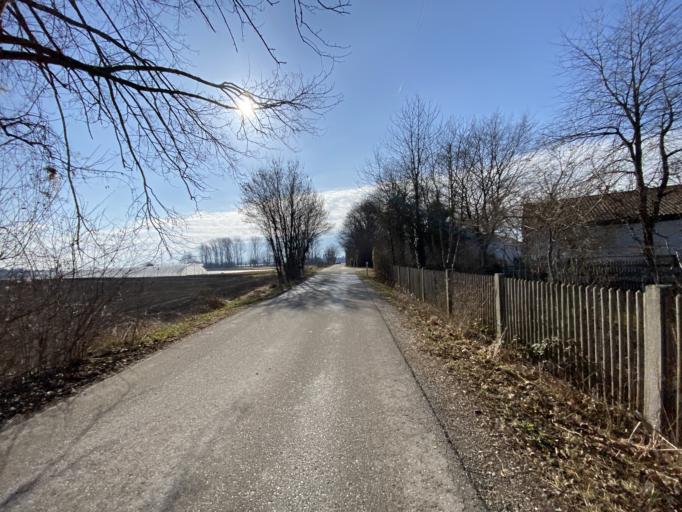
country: DE
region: Bavaria
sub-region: Upper Bavaria
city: Unterfoehring
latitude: 48.1637
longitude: 11.6492
